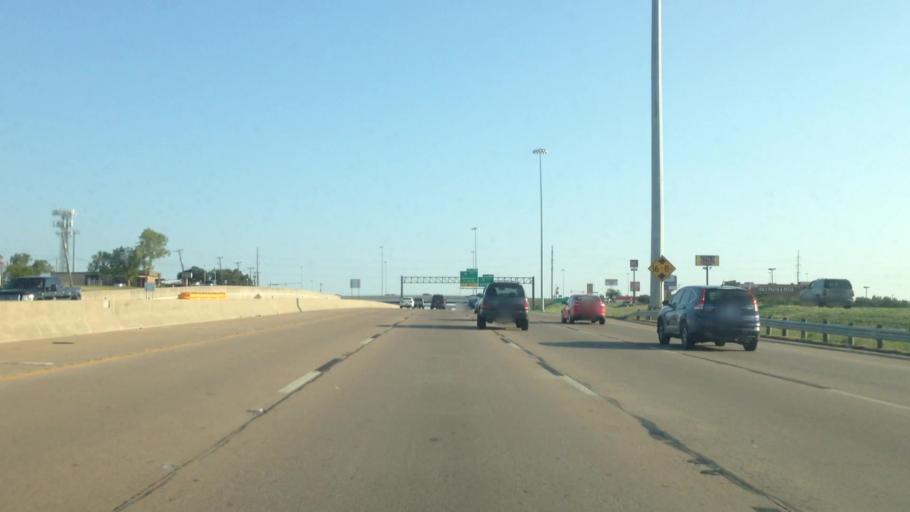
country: US
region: Texas
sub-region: Tarrant County
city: Richland Hills
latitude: 32.7702
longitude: -97.2129
